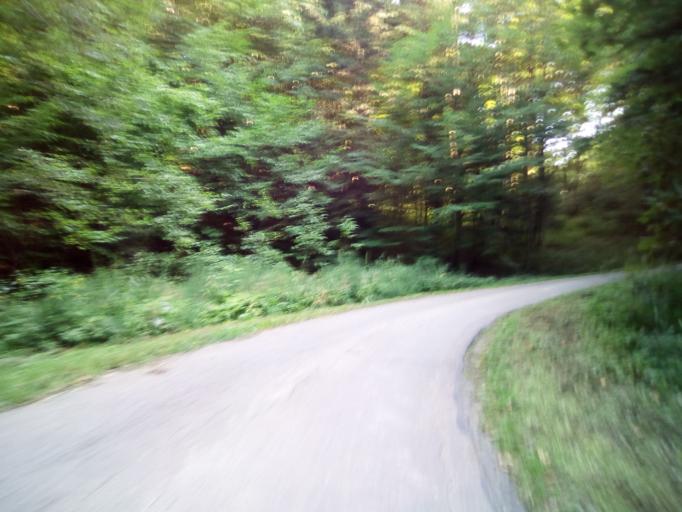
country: PL
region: Subcarpathian Voivodeship
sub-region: Powiat brzozowski
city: Domaradz
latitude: 49.8116
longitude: 21.9650
